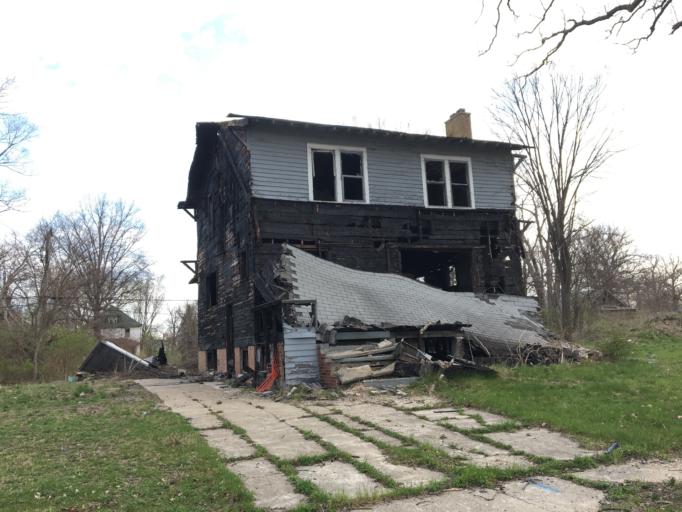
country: US
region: Michigan
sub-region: Oakland County
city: Hazel Park
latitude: 42.4361
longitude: -83.1153
